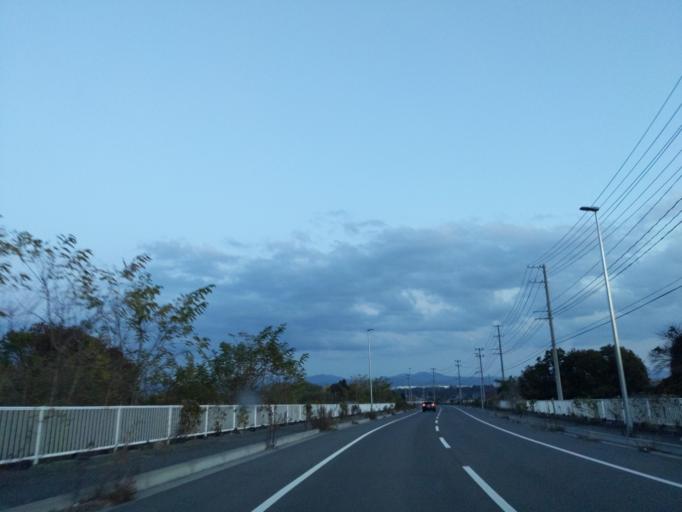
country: JP
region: Fukushima
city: Koriyama
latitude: 37.4612
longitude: 140.3062
